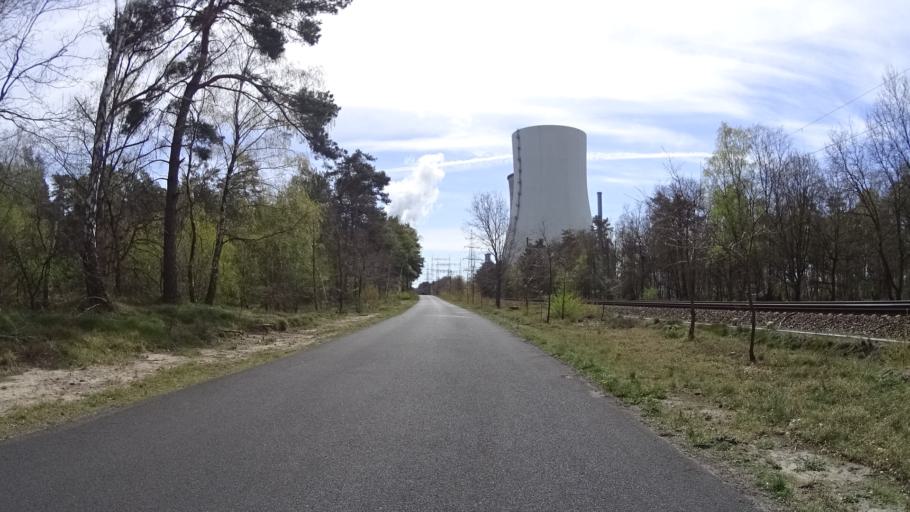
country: DE
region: Lower Saxony
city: Lingen
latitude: 52.4867
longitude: 7.3048
